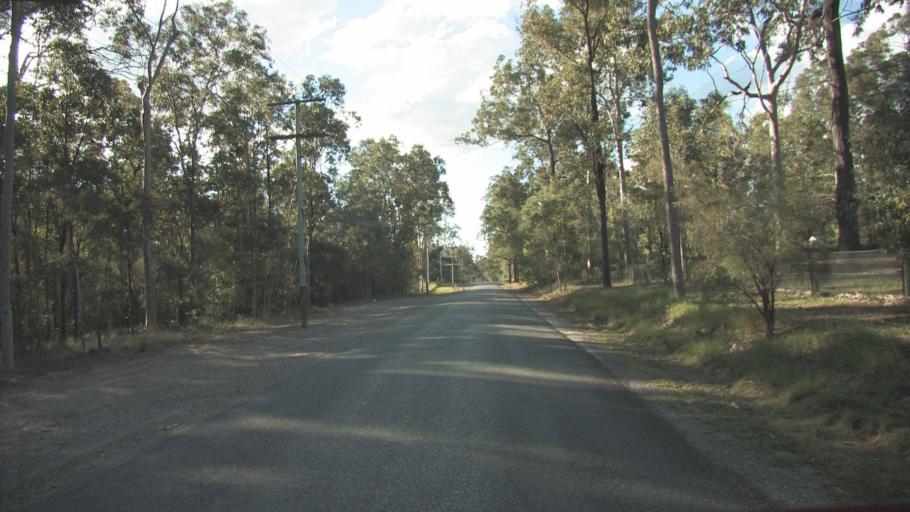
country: AU
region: Queensland
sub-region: Ipswich
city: Springfield Lakes
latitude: -27.6978
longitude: 152.9490
